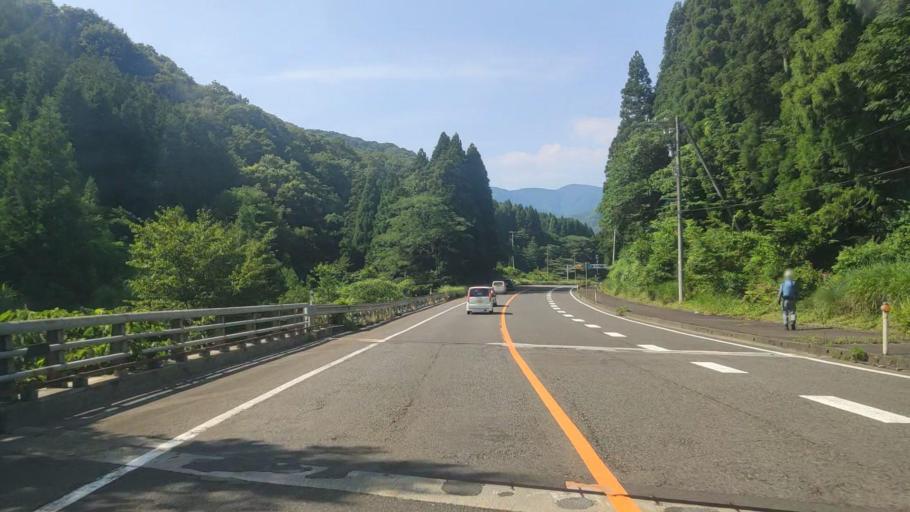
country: JP
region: Fukui
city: Tsuruga
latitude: 35.5949
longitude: 136.1230
